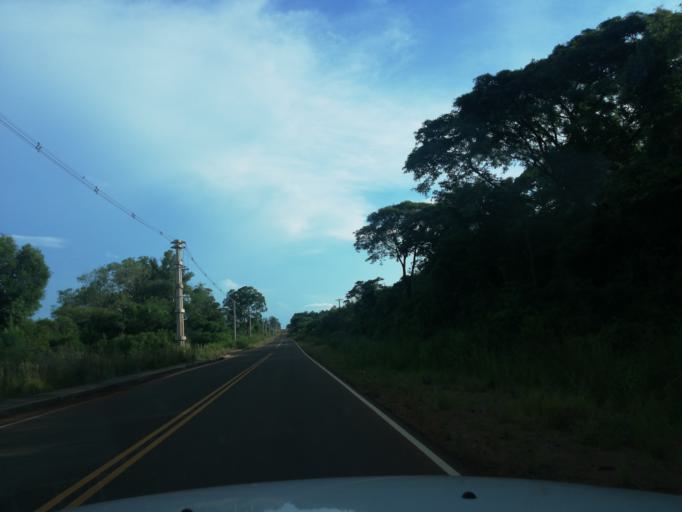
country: AR
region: Misiones
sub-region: Departamento de Candelaria
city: Candelaria
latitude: -27.4525
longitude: -55.7753
